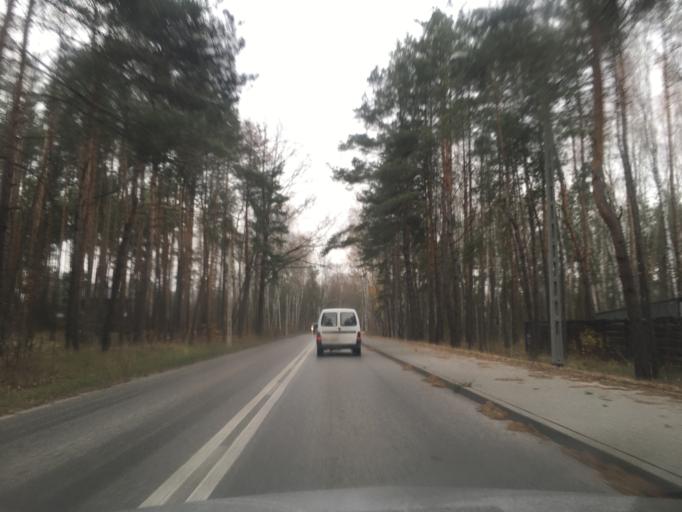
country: PL
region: Masovian Voivodeship
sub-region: Powiat piaseczynski
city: Lesznowola
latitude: 52.0609
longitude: 20.9195
